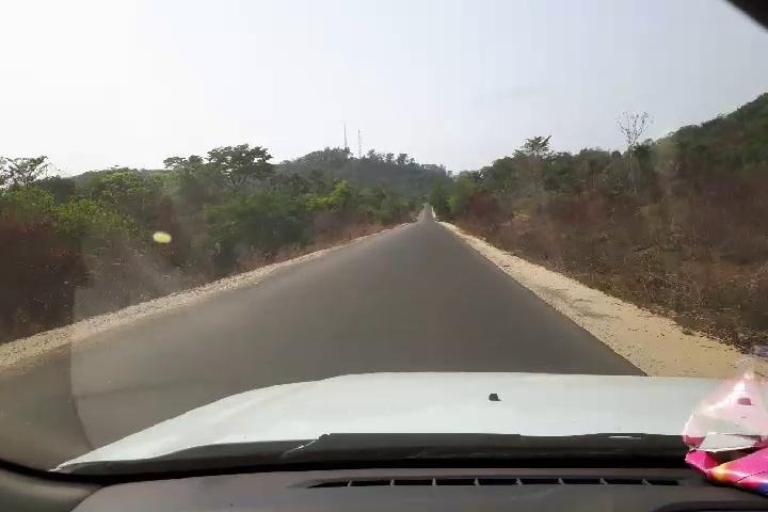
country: SL
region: Western Area
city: Waterloo
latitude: 8.2587
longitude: -13.1599
